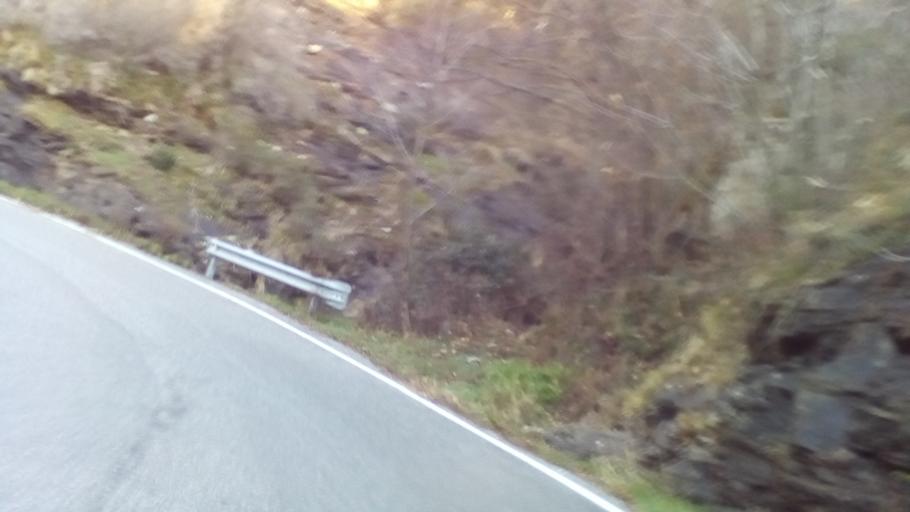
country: IT
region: Tuscany
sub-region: Provincia di Massa-Carrara
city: Montignoso
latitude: 44.0539
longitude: 10.1891
